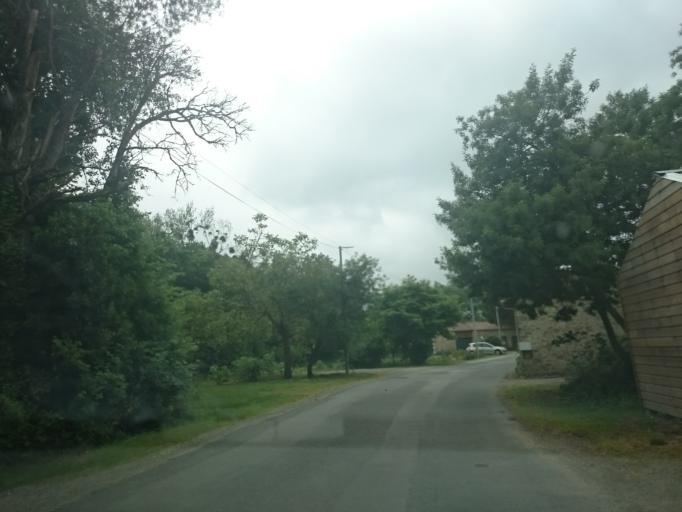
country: FR
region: Pays de la Loire
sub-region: Departement de la Loire-Atlantique
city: Bouaye
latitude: 47.1354
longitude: -1.6715
